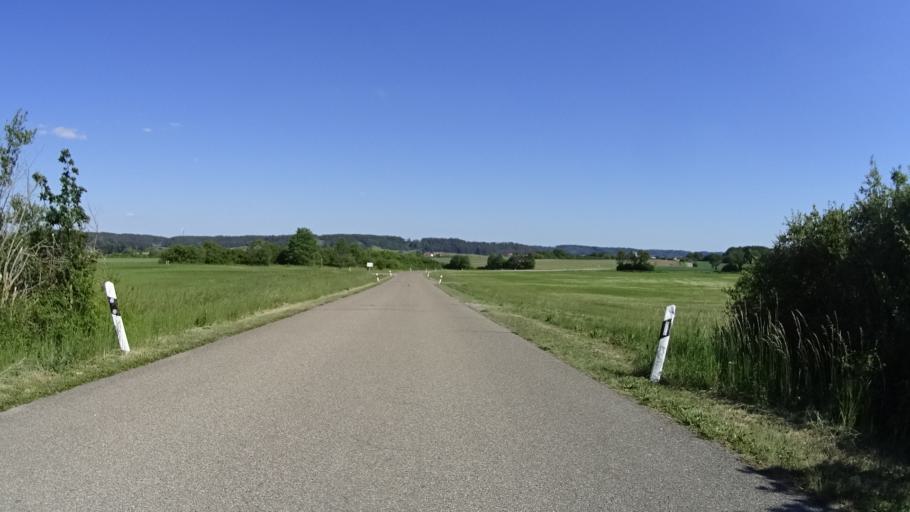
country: DE
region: Bavaria
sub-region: Regierungsbezirk Mittelfranken
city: Dombuhl
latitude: 49.2275
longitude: 10.2975
